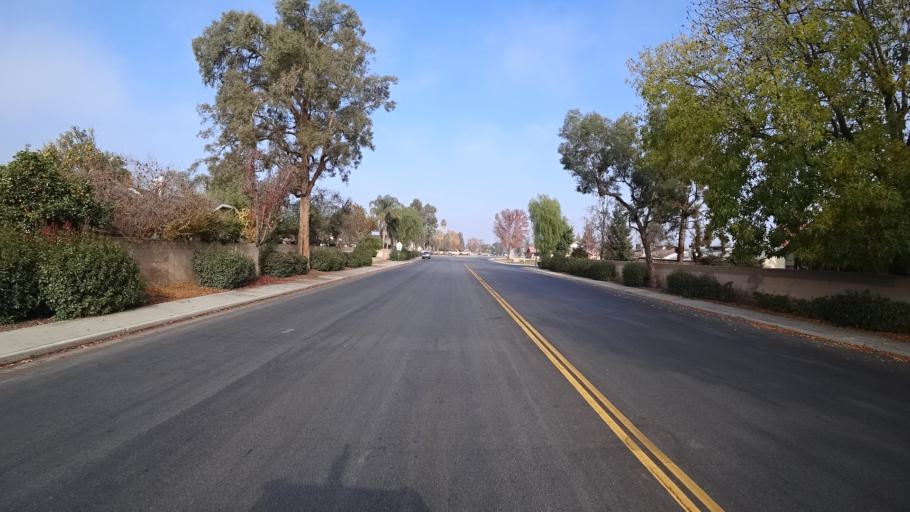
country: US
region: California
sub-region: Kern County
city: Greenacres
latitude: 35.3160
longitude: -119.0988
